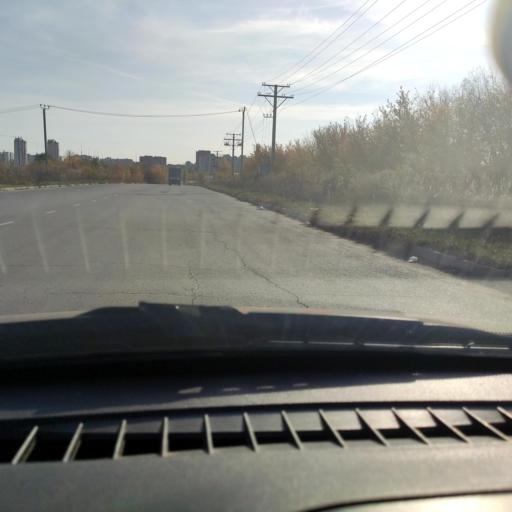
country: RU
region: Samara
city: Tol'yatti
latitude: 53.5556
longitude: 49.3289
